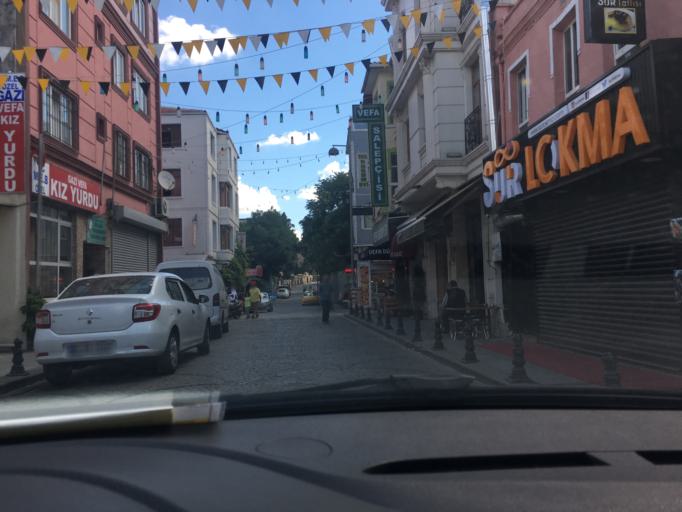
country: TR
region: Istanbul
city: Istanbul
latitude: 41.0155
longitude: 28.9586
